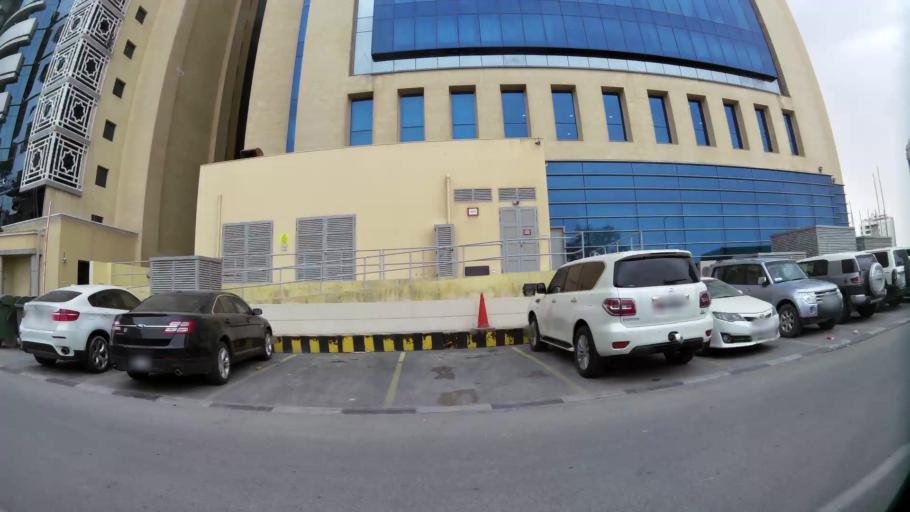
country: QA
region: Baladiyat ad Dawhah
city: Doha
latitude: 25.2904
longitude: 51.5428
